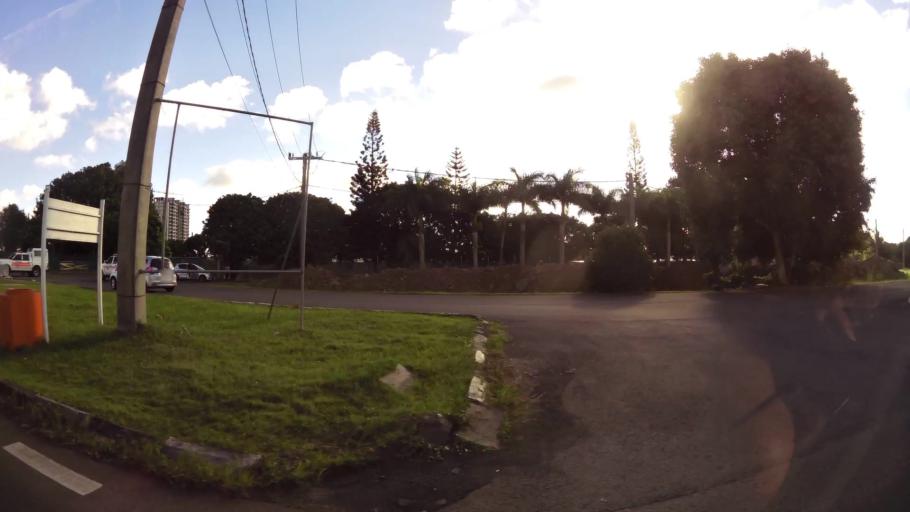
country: MU
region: Plaines Wilhems
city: Quatre Bornes
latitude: -20.2761
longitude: 57.4966
